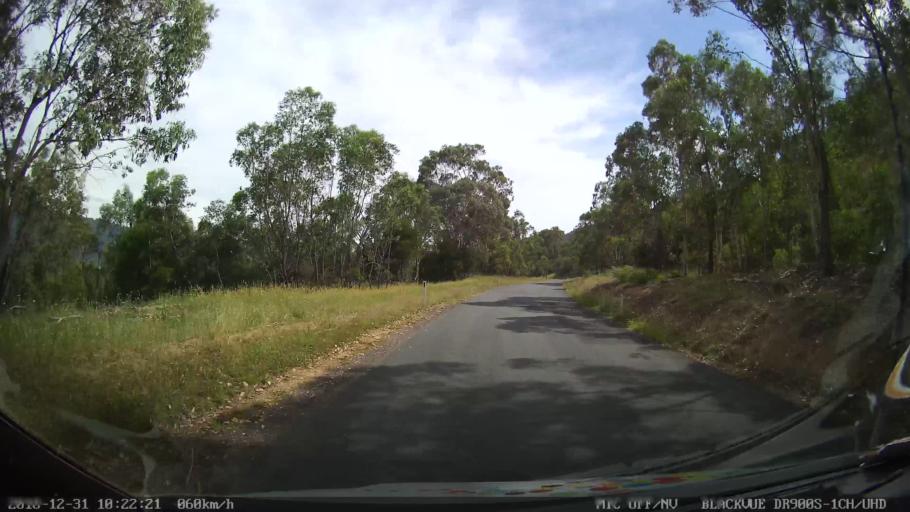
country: AU
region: New South Wales
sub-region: Snowy River
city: Jindabyne
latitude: -36.5263
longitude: 148.1428
